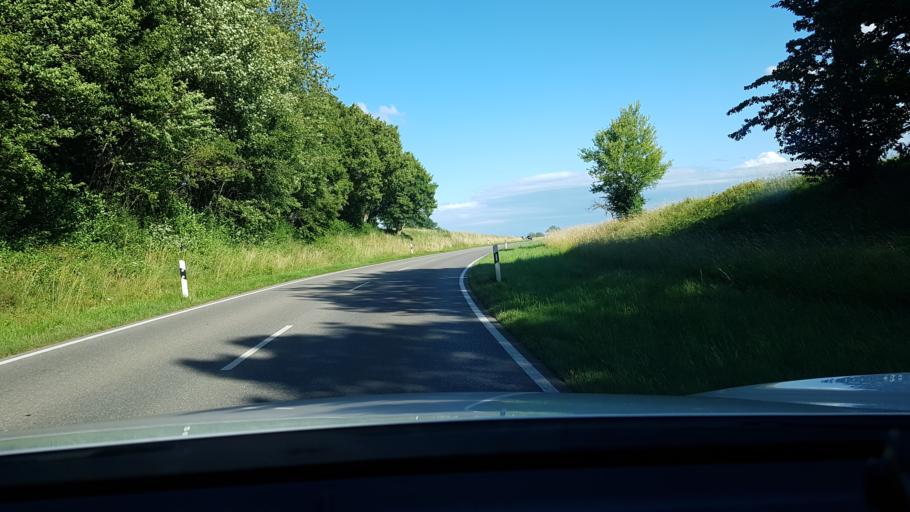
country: DE
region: Baden-Wuerttemberg
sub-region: Tuebingen Region
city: Mietingen
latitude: 48.1807
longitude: 9.9112
